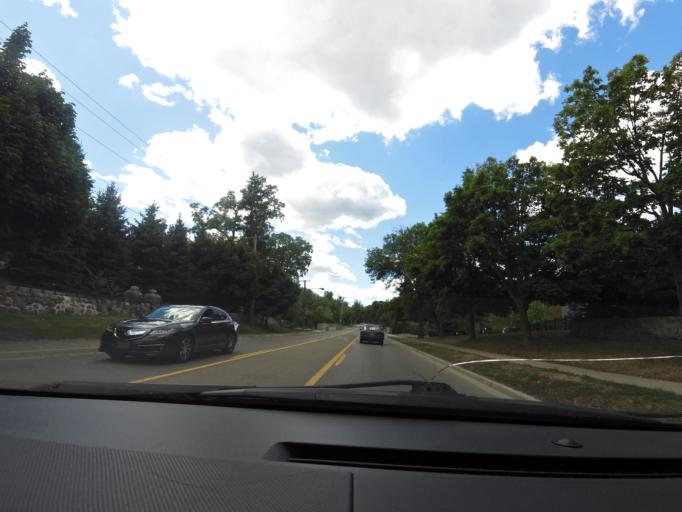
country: CA
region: Ontario
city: Burlington
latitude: 43.3394
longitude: -79.7688
